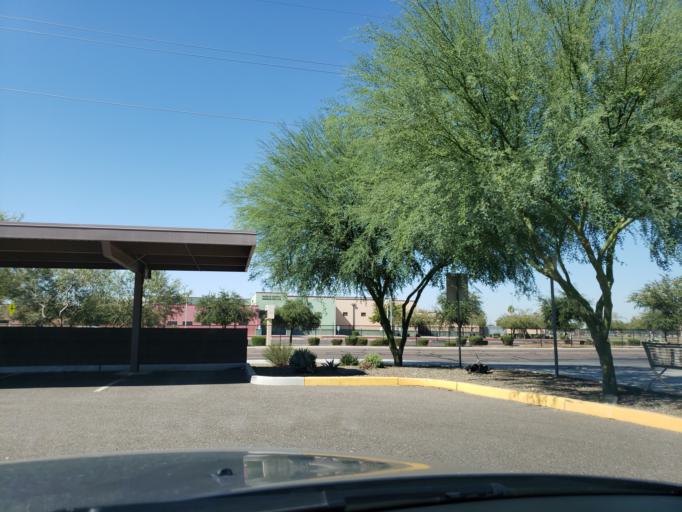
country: US
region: Arizona
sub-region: Maricopa County
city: Tolleson
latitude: 33.4784
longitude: -112.2288
